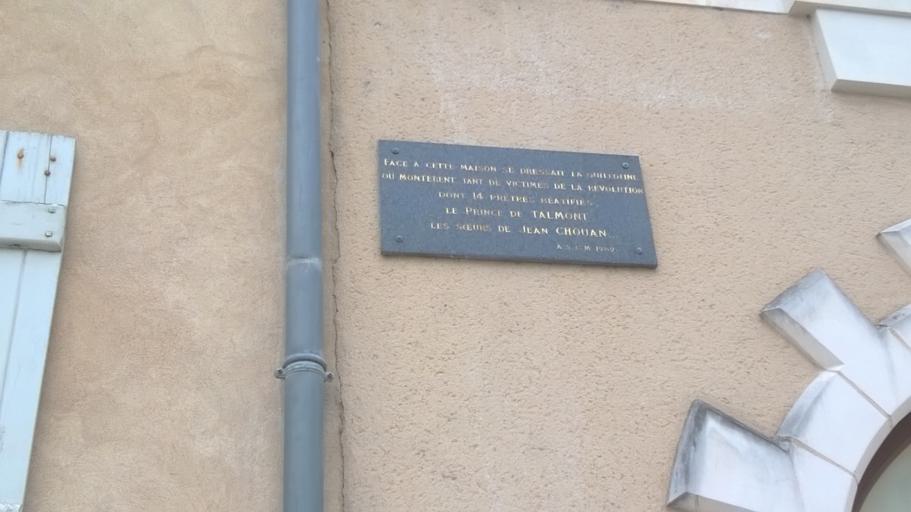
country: FR
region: Pays de la Loire
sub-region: Departement de la Mayenne
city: Laval
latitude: 48.0689
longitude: -0.7727
